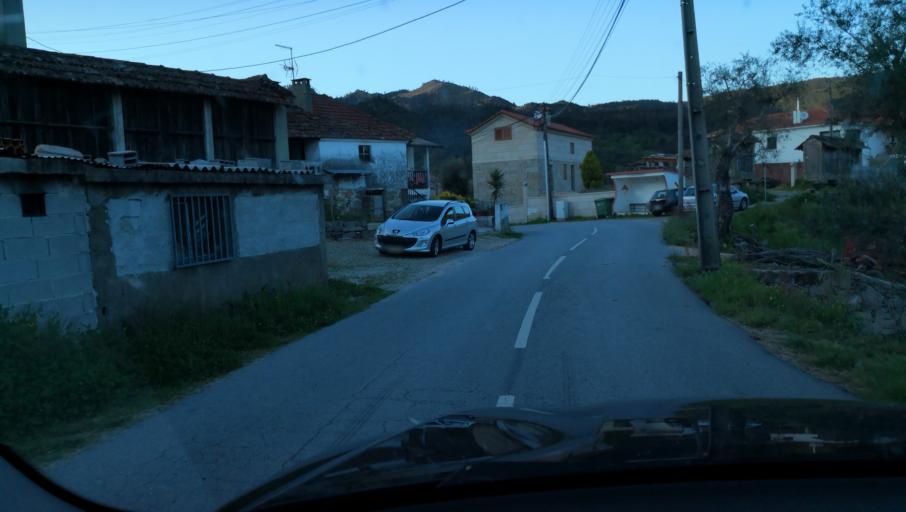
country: PT
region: Vila Real
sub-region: Mondim de Basto
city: Mondim de Basto
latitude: 41.4155
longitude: -7.8866
